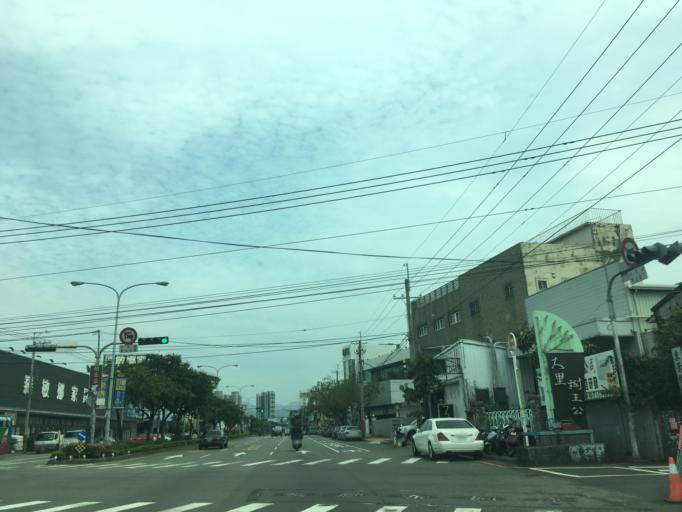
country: TW
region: Taiwan
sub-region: Taichung City
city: Taichung
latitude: 24.1055
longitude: 120.6667
